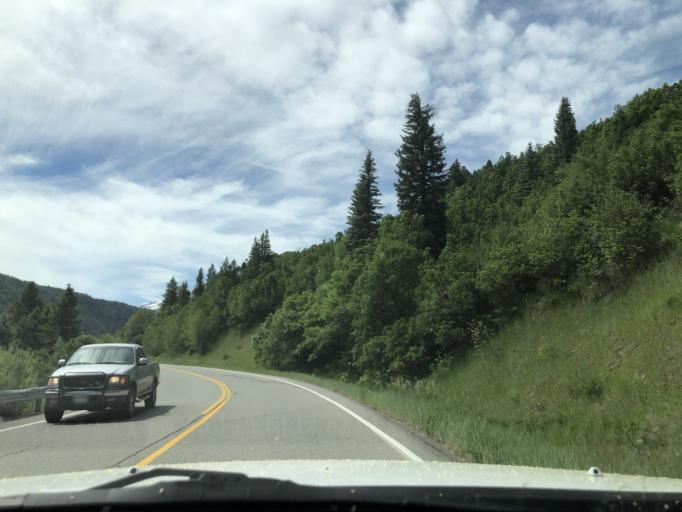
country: US
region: Colorado
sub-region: Delta County
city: Paonia
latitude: 38.9782
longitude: -107.3443
